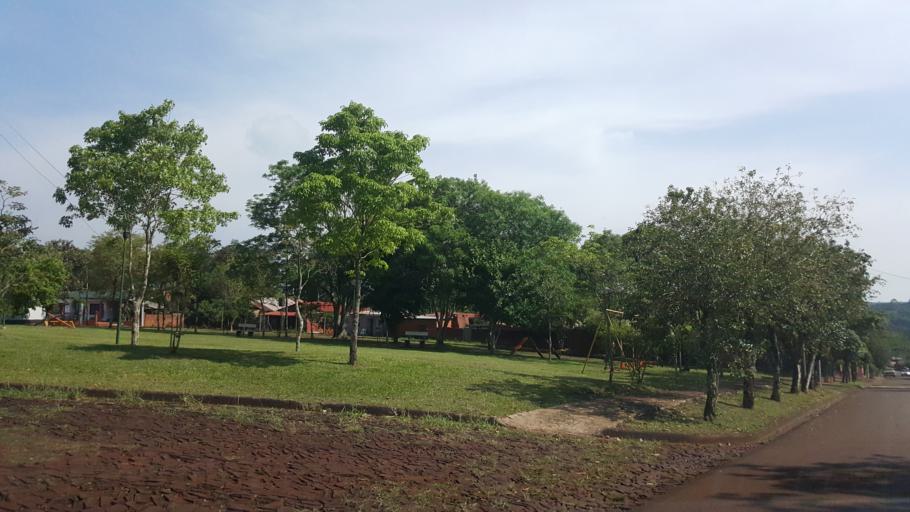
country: AR
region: Misiones
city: Capiovi
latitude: -26.9302
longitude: -55.0555
